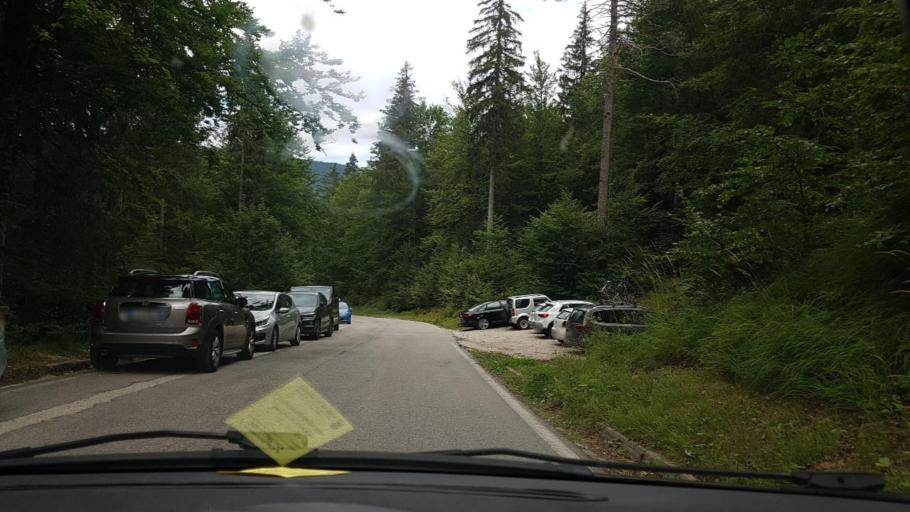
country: AT
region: Carinthia
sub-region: Politischer Bezirk Villach Land
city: Arnoldstein
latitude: 46.4779
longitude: 13.6728
